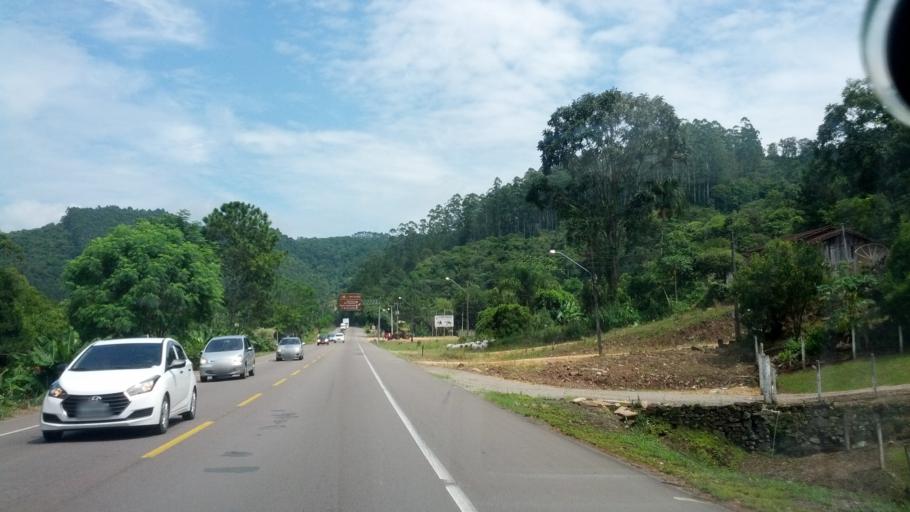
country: BR
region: Santa Catarina
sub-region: Ibirama
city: Ibirama
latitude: -27.0783
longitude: -49.4898
